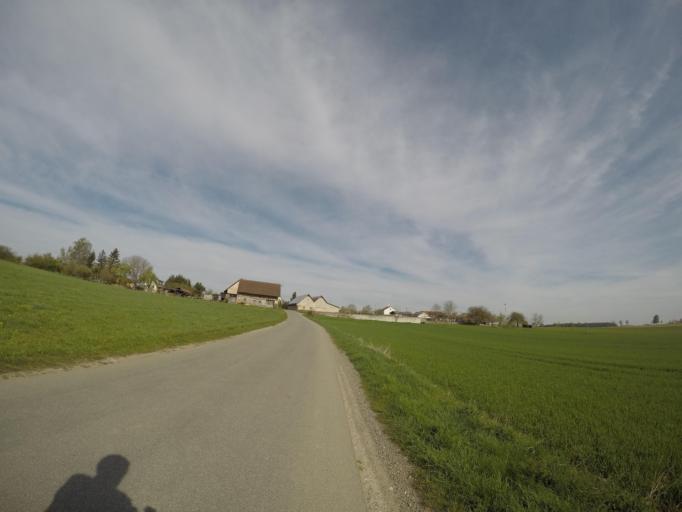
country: DE
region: Baden-Wuerttemberg
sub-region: Tuebingen Region
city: Allmannsweiler
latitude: 48.0018
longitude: 9.5778
